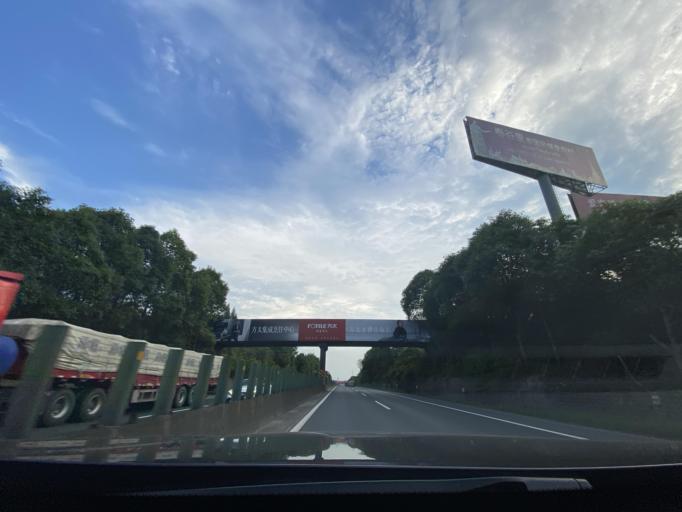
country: CN
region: Sichuan
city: Luojiang
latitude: 31.3943
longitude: 104.5612
